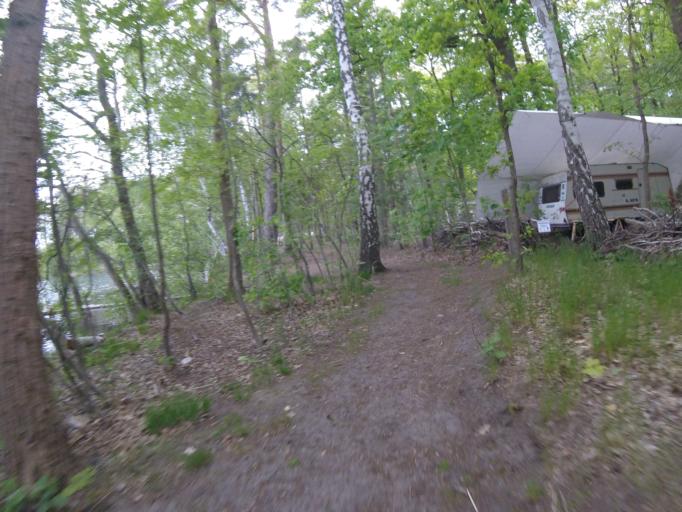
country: DE
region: Brandenburg
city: Bestensee
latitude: 52.2527
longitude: 13.6693
